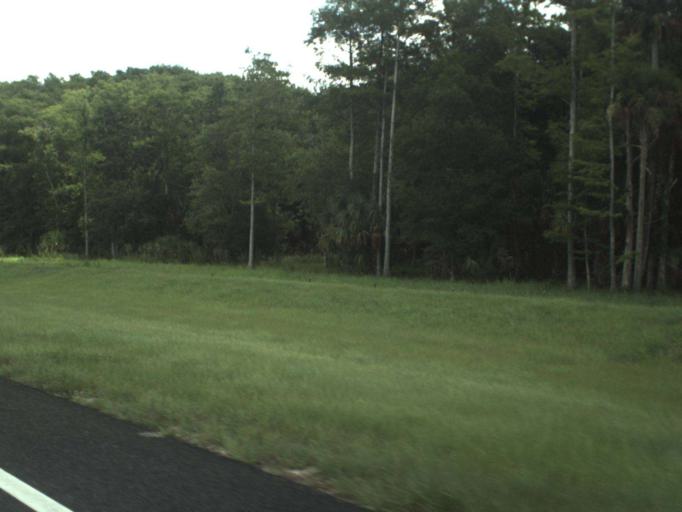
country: US
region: Florida
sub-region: Okeechobee County
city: Taylor Creek
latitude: 27.3313
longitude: -80.6507
